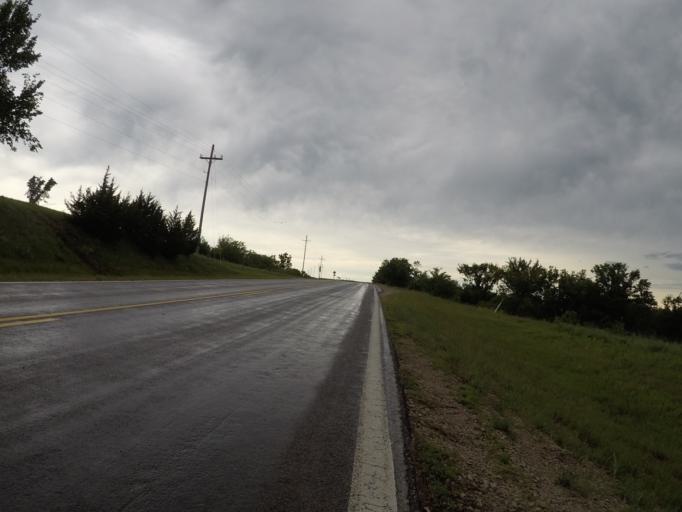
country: US
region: Kansas
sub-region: Wabaunsee County
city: Alma
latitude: 38.8613
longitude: -96.1135
